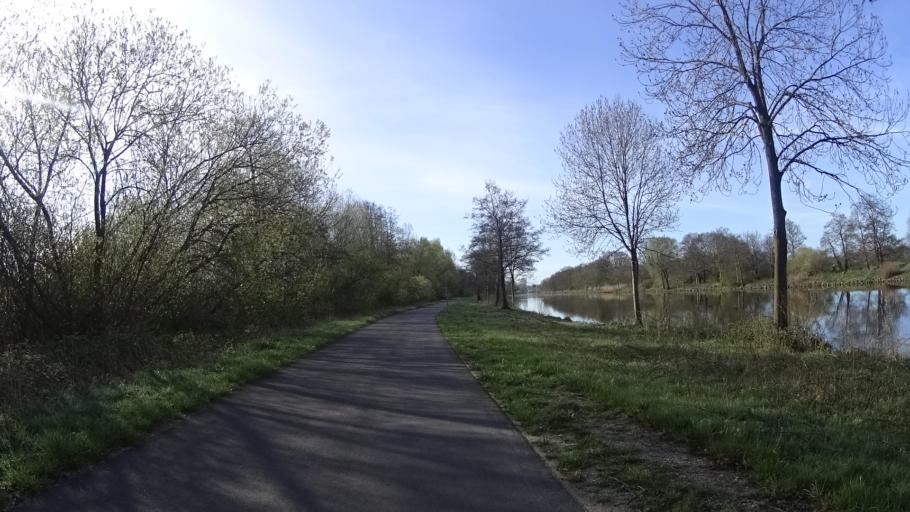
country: DE
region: Lower Saxony
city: Haren
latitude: 52.8054
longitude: 7.2596
